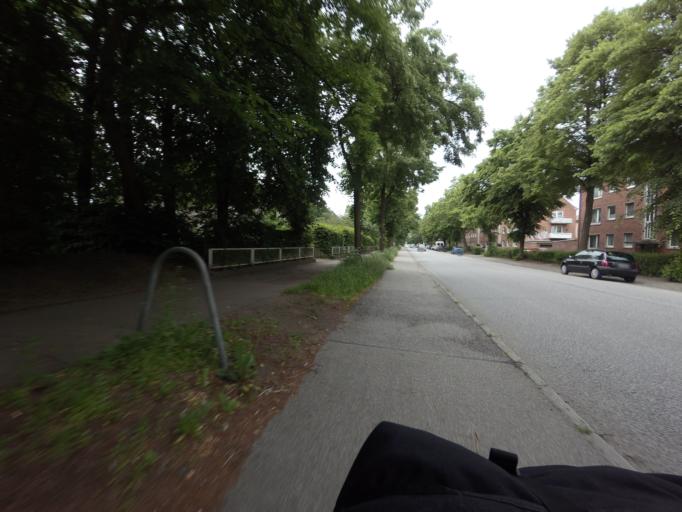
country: DE
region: Mecklenburg-Vorpommern
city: Selmsdorf
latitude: 53.9069
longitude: 10.8035
